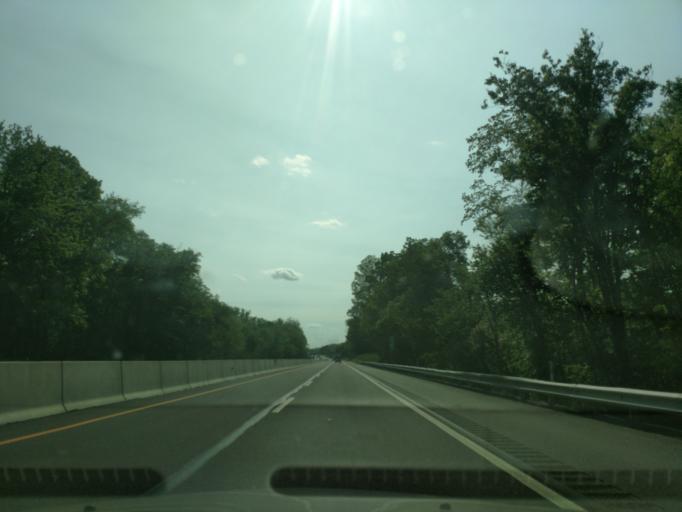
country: US
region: Pennsylvania
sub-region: Lancaster County
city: Clay
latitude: 40.2425
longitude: -76.2421
